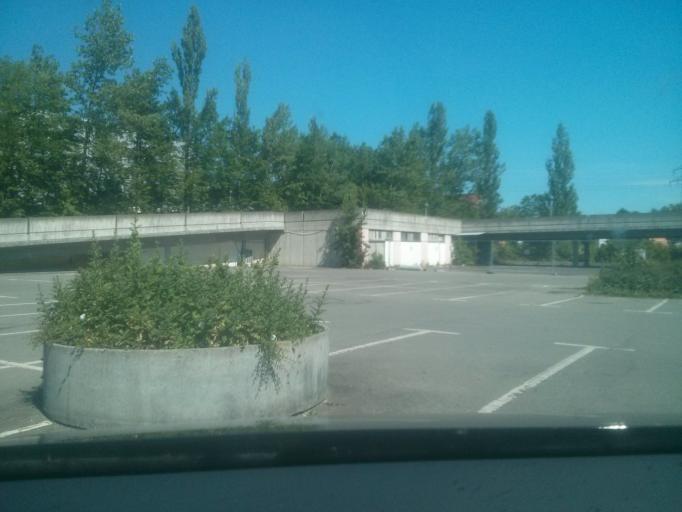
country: DE
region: Baden-Wuerttemberg
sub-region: Tuebingen Region
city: Wannweil
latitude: 48.4968
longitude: 9.1565
